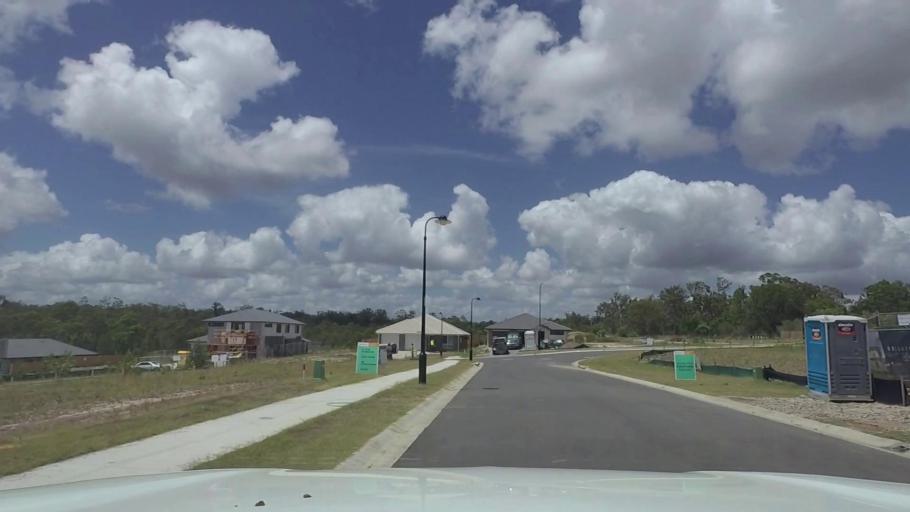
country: AU
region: Queensland
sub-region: Logan
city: Park Ridge South
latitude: -27.6905
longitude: 153.0548
